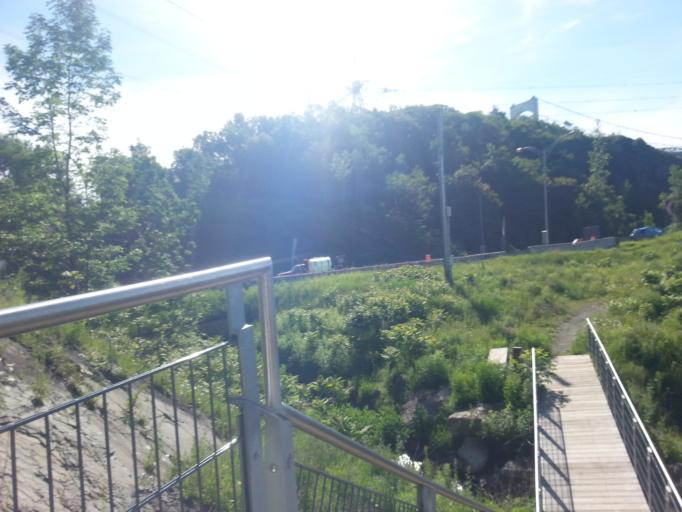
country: CA
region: Quebec
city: L'Ancienne-Lorette
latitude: 46.7498
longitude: -71.2995
